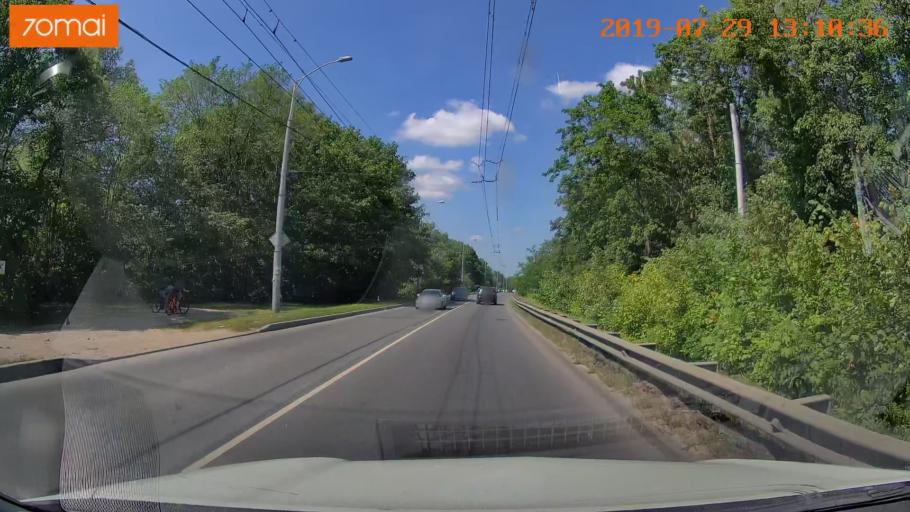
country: RU
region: Kaliningrad
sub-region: Gorod Kaliningrad
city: Kaliningrad
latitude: 54.7160
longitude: 20.4015
